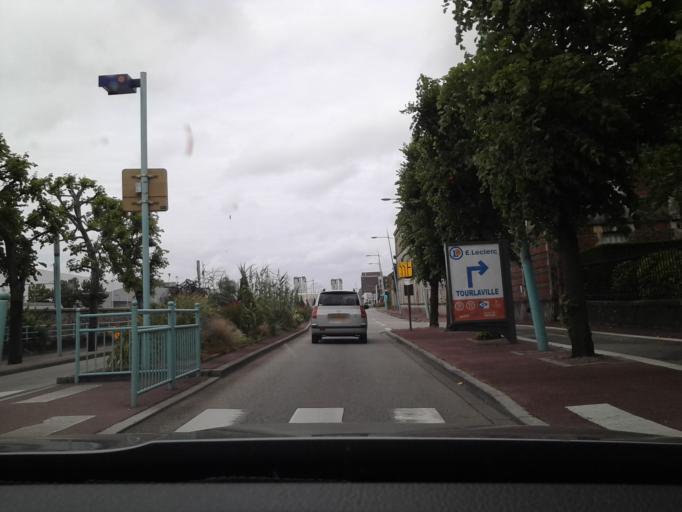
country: FR
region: Lower Normandy
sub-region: Departement de la Manche
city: Cherbourg-Octeville
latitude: 49.6320
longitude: -1.6176
